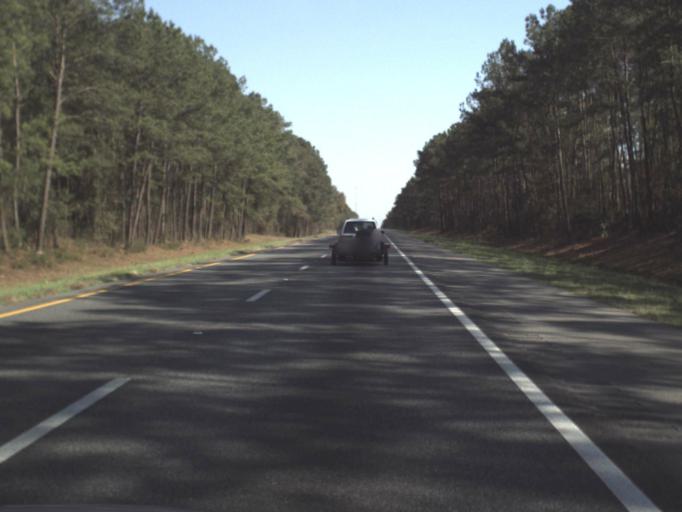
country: US
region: Florida
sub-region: Gadsden County
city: Midway
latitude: 30.5138
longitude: -84.4768
